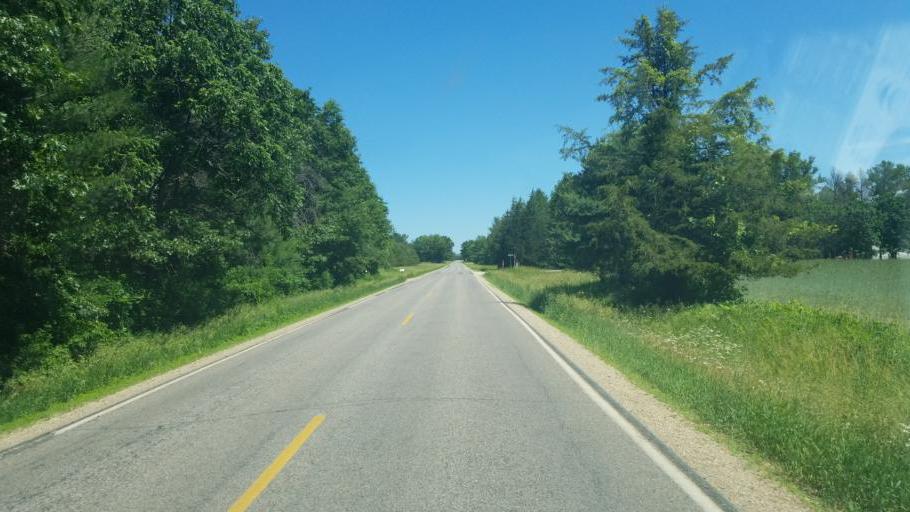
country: US
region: Wisconsin
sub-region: Adams County
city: Adams
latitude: 43.8829
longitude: -89.9383
